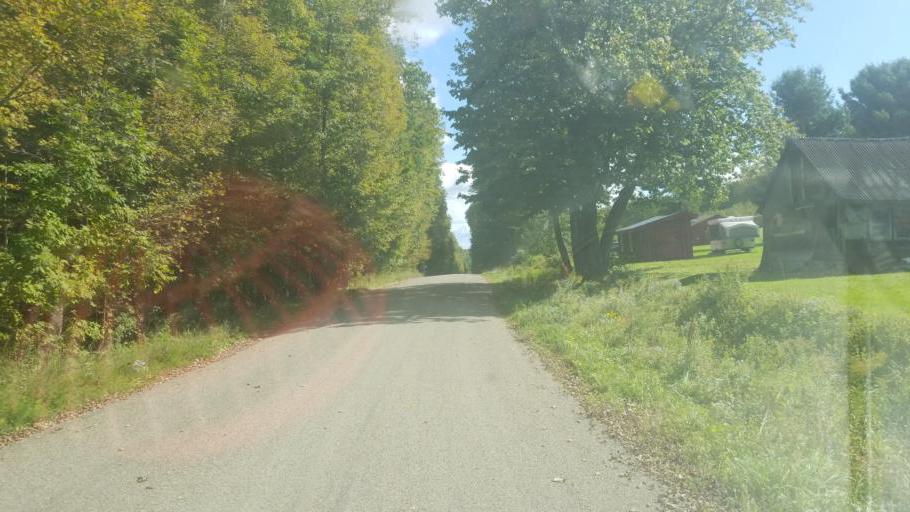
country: US
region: New York
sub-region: Allegany County
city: Cuba
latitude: 42.1928
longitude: -78.3229
